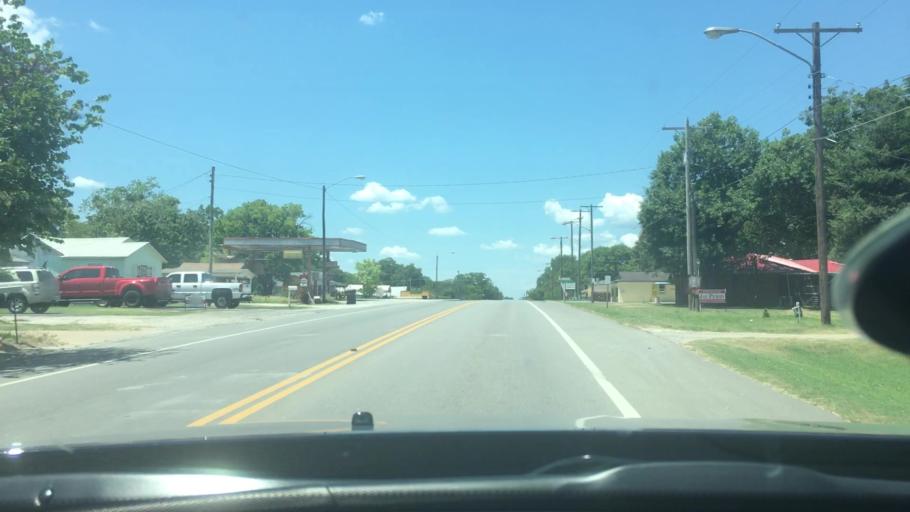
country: US
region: Oklahoma
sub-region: Bryan County
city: Durant
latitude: 34.0166
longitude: -96.1345
